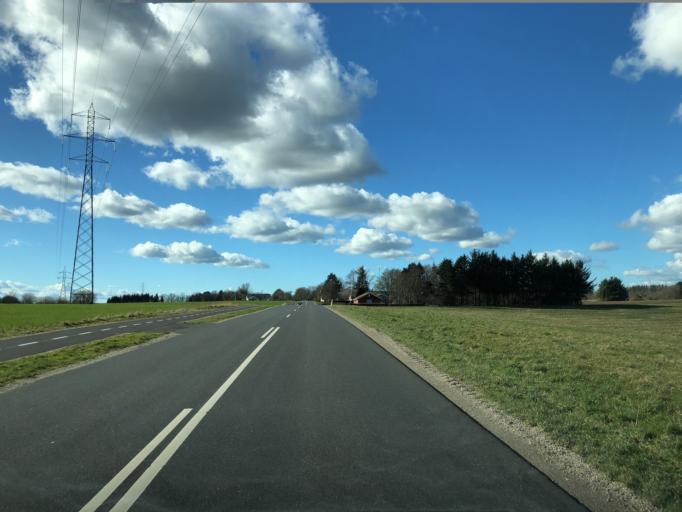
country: DK
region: Central Jutland
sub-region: Favrskov Kommune
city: Hinnerup
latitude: 56.2820
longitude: 10.0289
